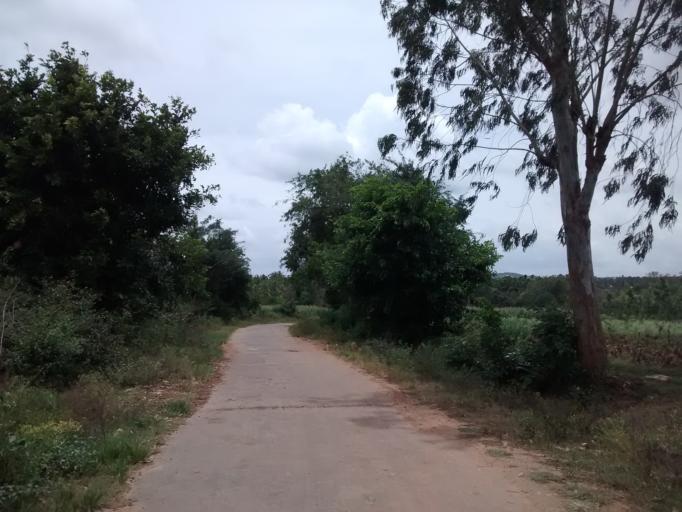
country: IN
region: Karnataka
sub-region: Hassan
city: Hassan
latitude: 12.9168
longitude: 76.1308
